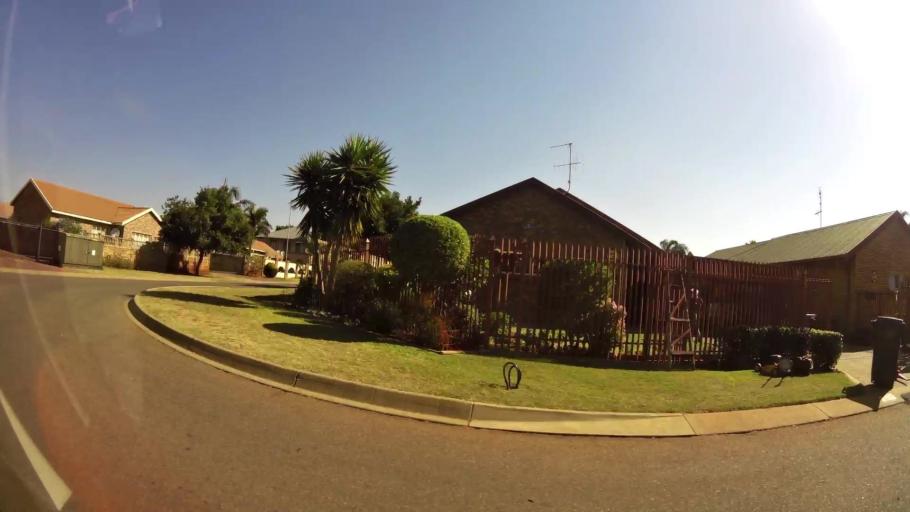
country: ZA
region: Gauteng
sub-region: City of Tshwane Metropolitan Municipality
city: Pretoria
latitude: -25.6591
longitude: 28.2586
